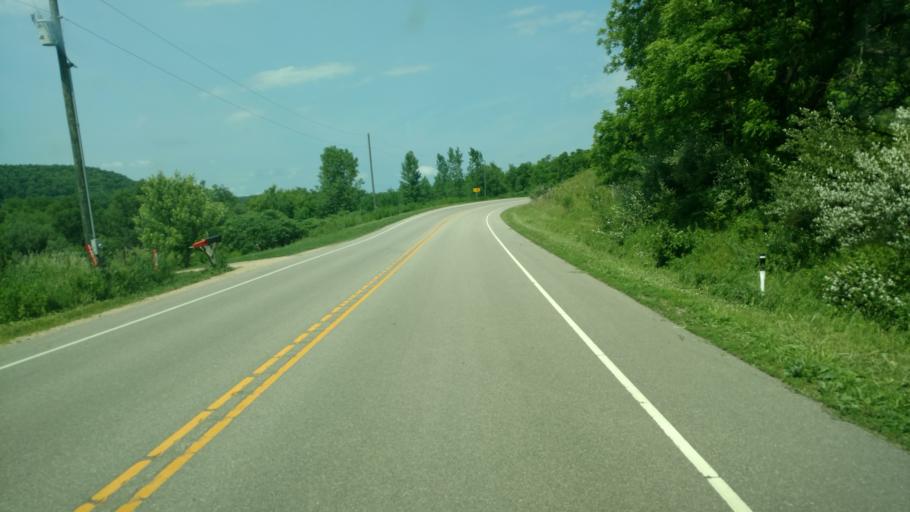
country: US
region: Wisconsin
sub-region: Vernon County
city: Viroqua
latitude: 43.4850
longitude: -90.6906
